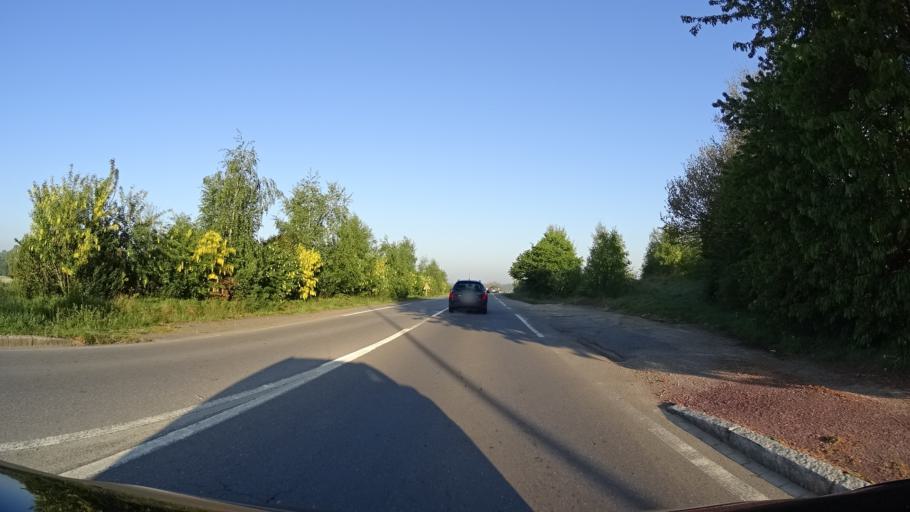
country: FR
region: Brittany
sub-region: Departement d'Ille-et-Vilaine
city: Bruz
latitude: 48.0261
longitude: -1.7656
